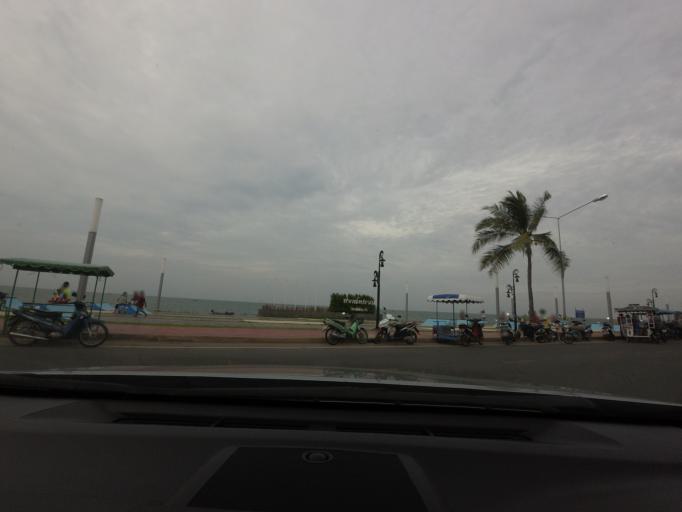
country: TH
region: Prachuap Khiri Khan
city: Pran Buri
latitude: 12.3876
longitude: 99.9982
